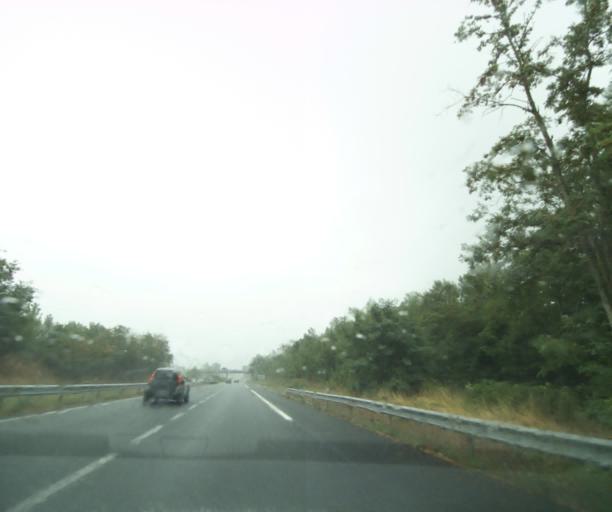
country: FR
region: Midi-Pyrenees
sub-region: Departement du Tarn
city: Brens
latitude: 43.8750
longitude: 1.9036
